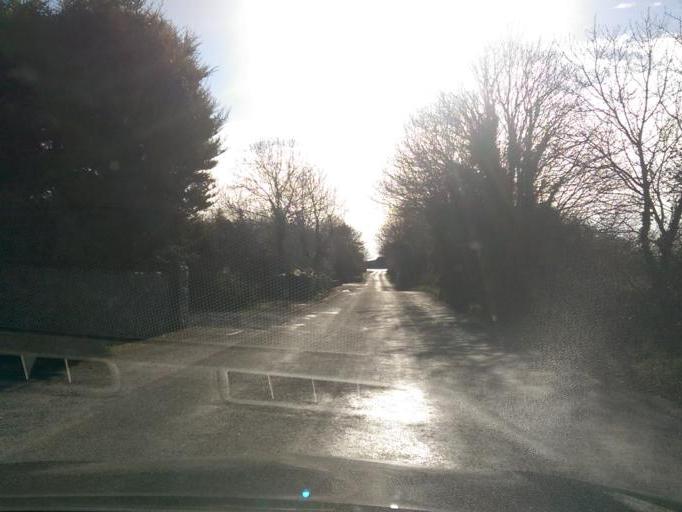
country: IE
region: Connaught
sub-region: County Galway
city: Oranmore
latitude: 53.2354
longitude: -8.9480
